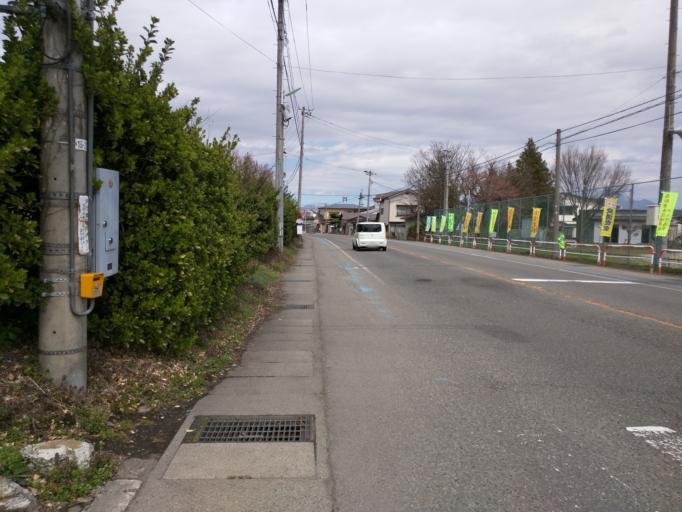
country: JP
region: Fukushima
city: Kitakata
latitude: 37.4600
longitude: 139.8426
